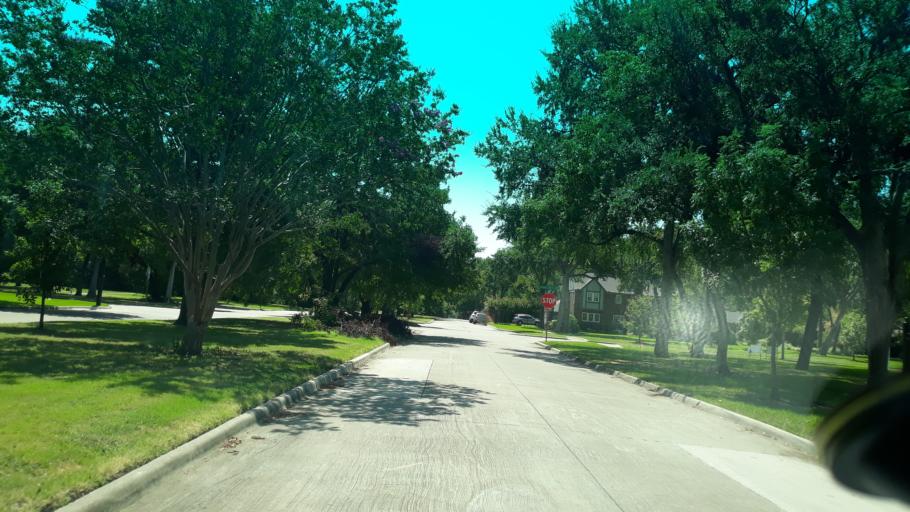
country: US
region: Texas
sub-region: Dallas County
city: Highland Park
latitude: 32.8146
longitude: -96.7177
